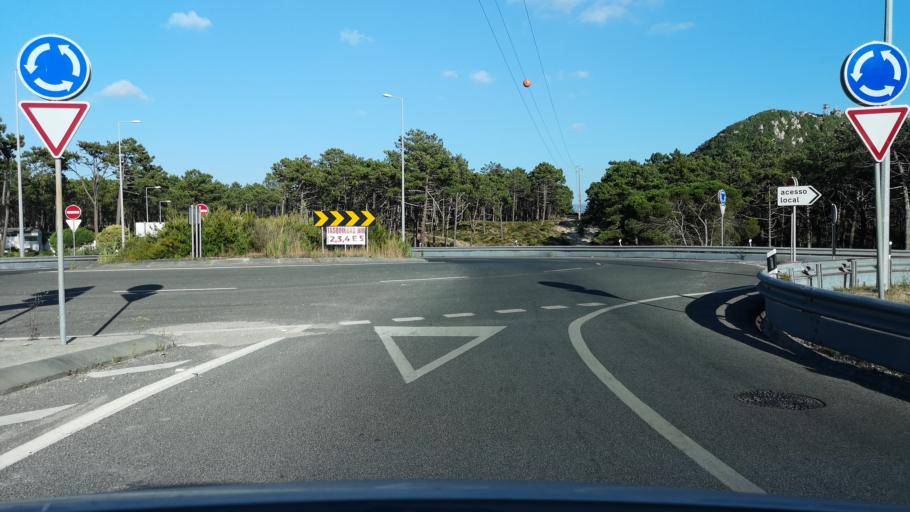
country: PT
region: Leiria
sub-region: Nazare
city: Nazare
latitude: 39.5976
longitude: -9.0567
